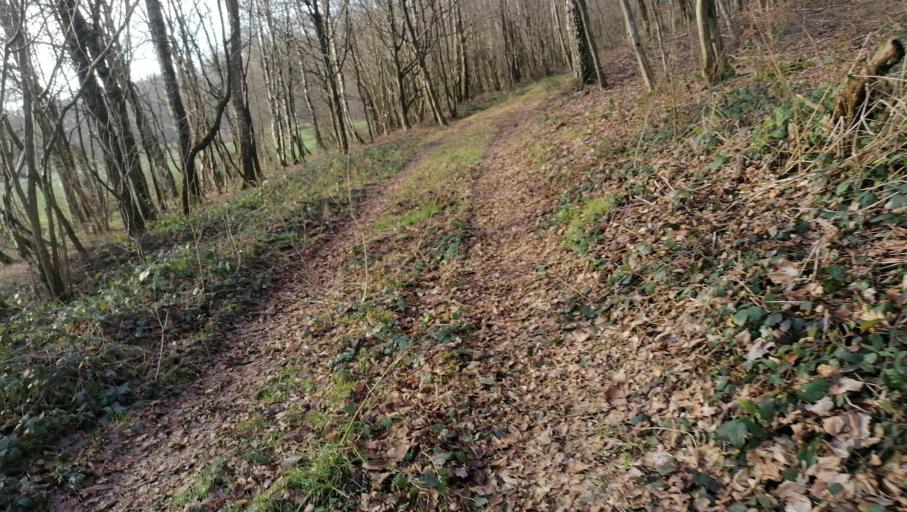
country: FR
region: Nord-Pas-de-Calais
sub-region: Departement du Nord
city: Ferriere-la-Grande
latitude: 50.2072
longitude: 4.0552
